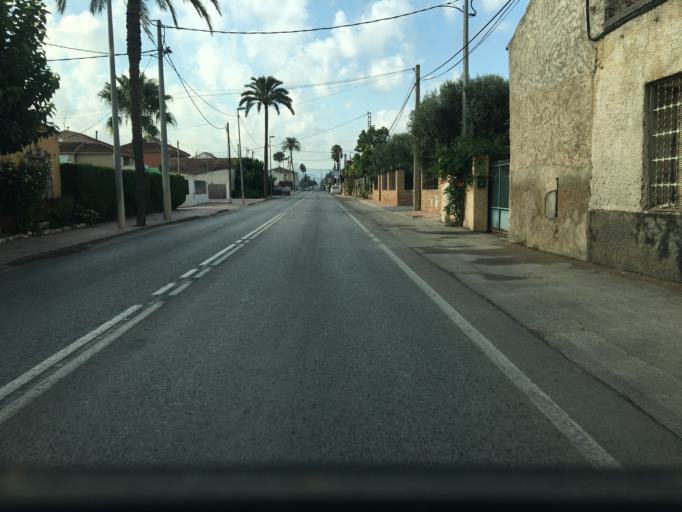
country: ES
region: Murcia
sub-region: Murcia
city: Santomera
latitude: 38.0347
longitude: -1.0438
